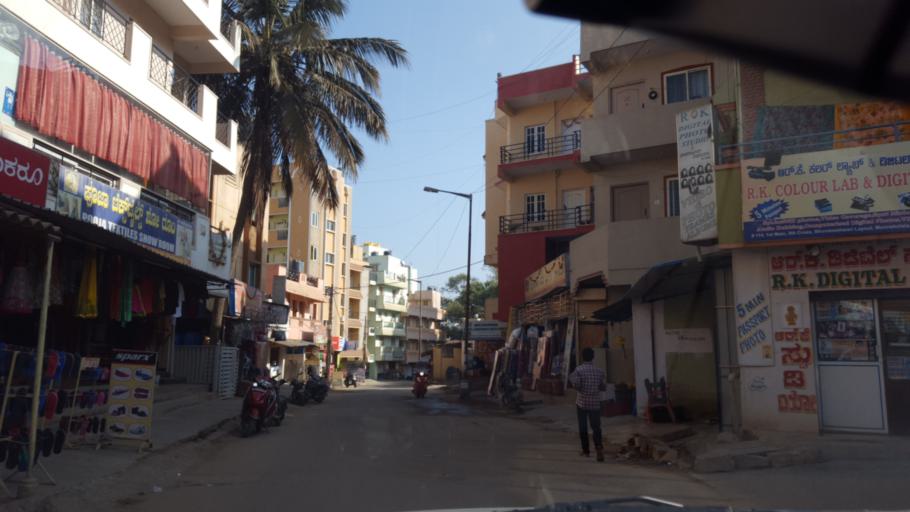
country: IN
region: Karnataka
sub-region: Bangalore Urban
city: Bangalore
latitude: 12.9498
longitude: 77.7074
